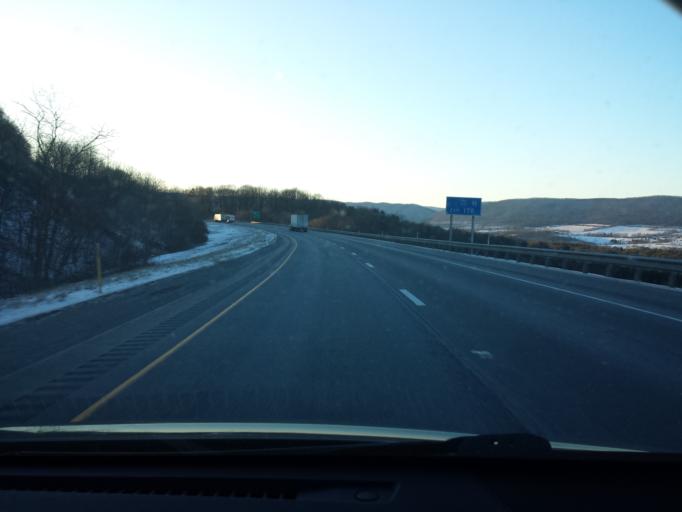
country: US
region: Pennsylvania
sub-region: Clinton County
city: Castanea
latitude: 41.0693
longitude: -77.4049
